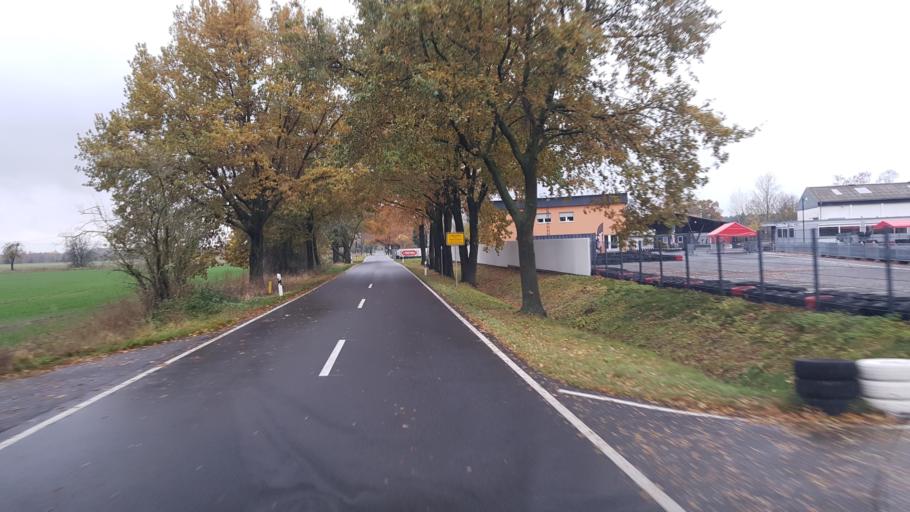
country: DE
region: Brandenburg
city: Drebkau
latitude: 51.6627
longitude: 14.2583
